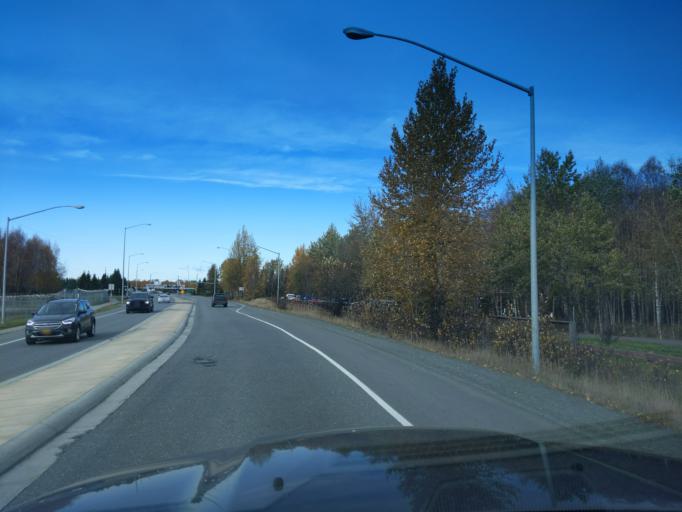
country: US
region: Alaska
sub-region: Anchorage Municipality
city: Anchorage
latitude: 61.1707
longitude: -149.9390
